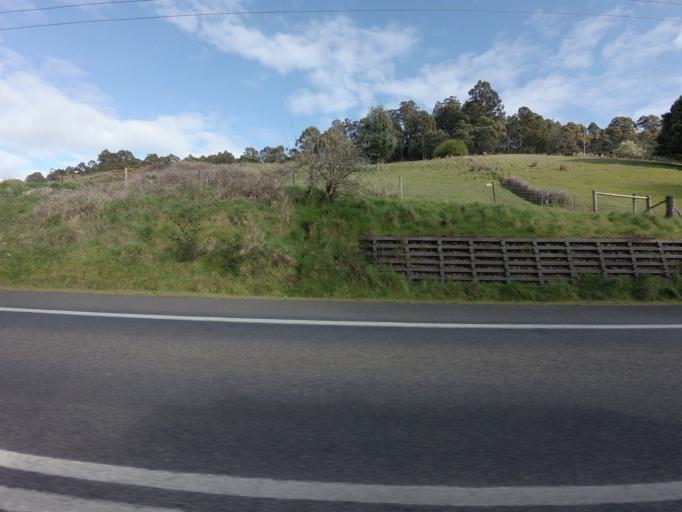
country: AU
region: Tasmania
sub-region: Huon Valley
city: Franklin
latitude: -43.1011
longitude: 147.0035
